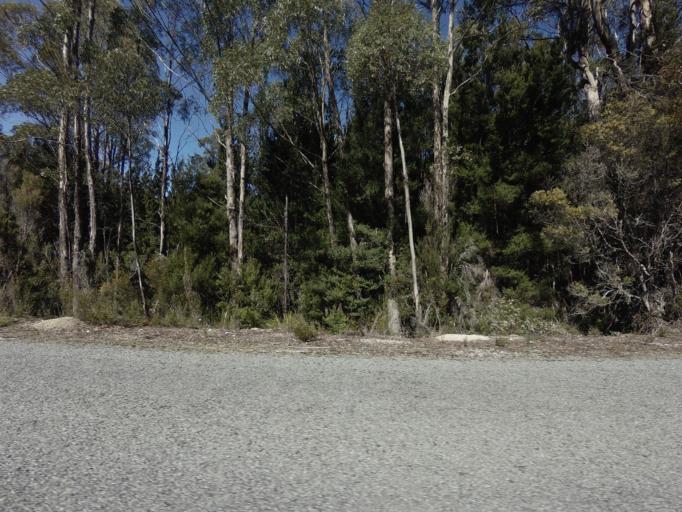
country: AU
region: Tasmania
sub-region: Huon Valley
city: Geeveston
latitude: -42.7689
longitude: 146.3971
